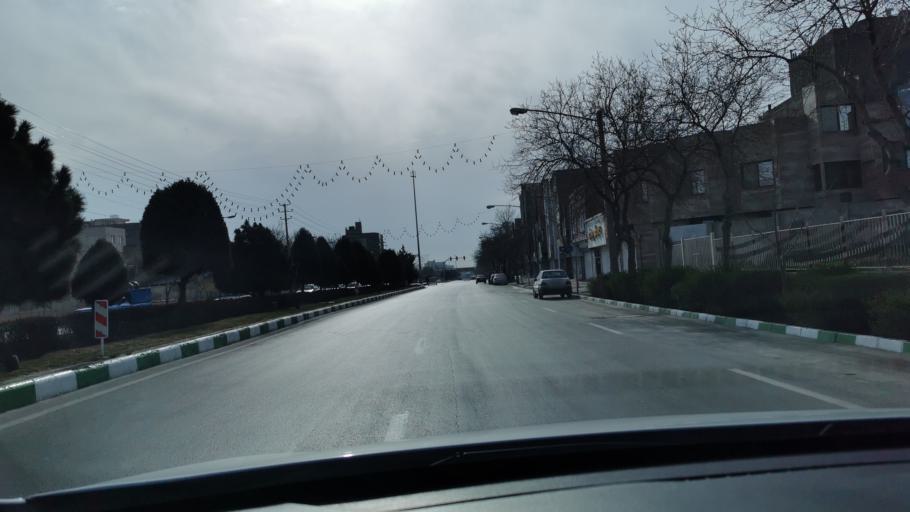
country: IR
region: Razavi Khorasan
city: Mashhad
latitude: 36.2996
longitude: 59.5231
